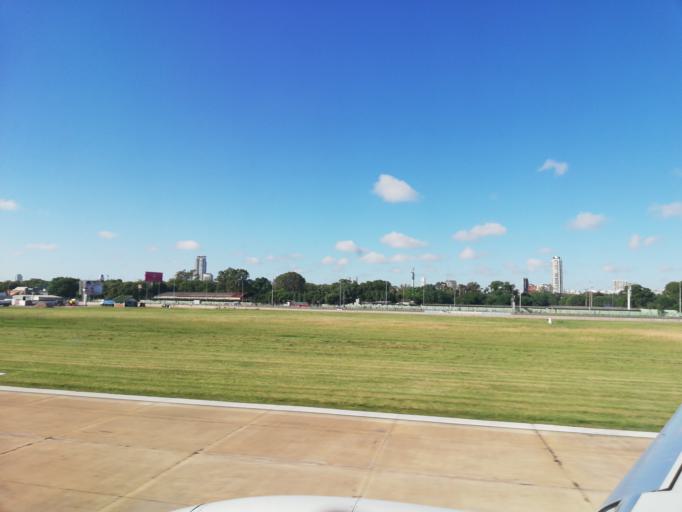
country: AR
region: Buenos Aires F.D.
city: Colegiales
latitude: -34.5573
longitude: -58.4194
